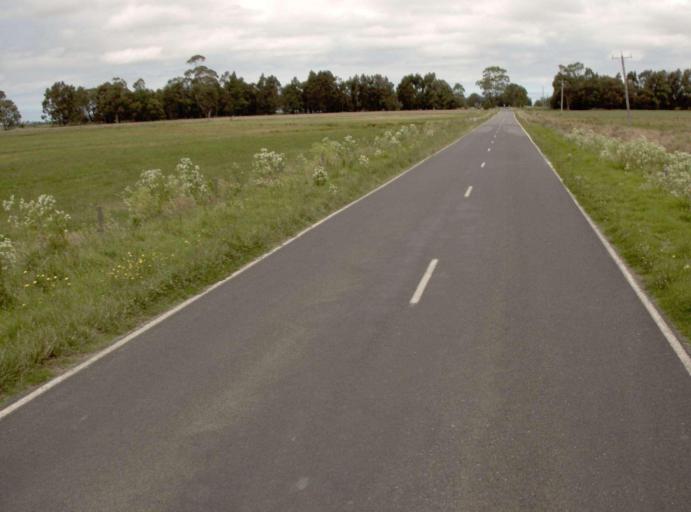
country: AU
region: Victoria
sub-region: Latrobe
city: Traralgon
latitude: -38.5064
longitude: 146.6638
